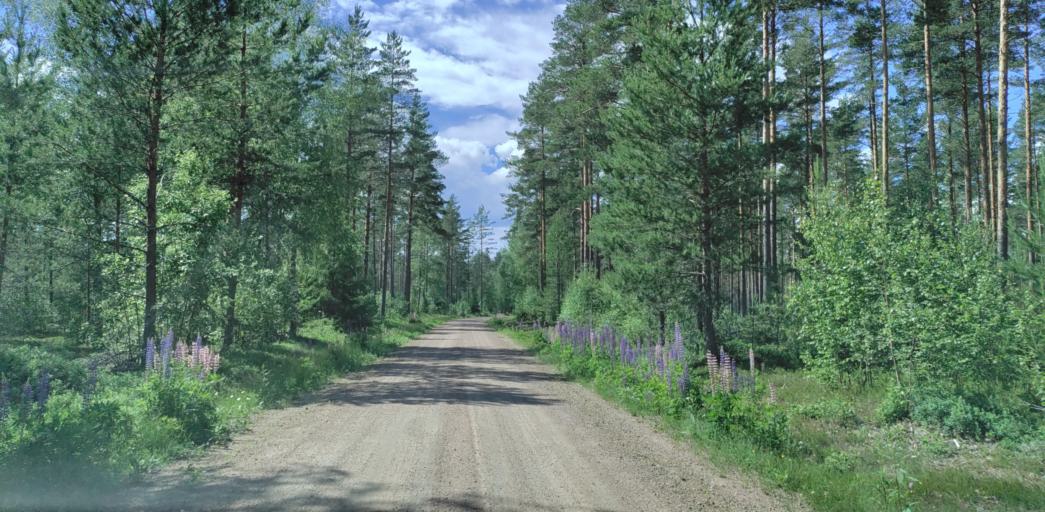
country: SE
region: Vaermland
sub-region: Munkfors Kommun
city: Munkfors
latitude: 59.9610
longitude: 13.5128
